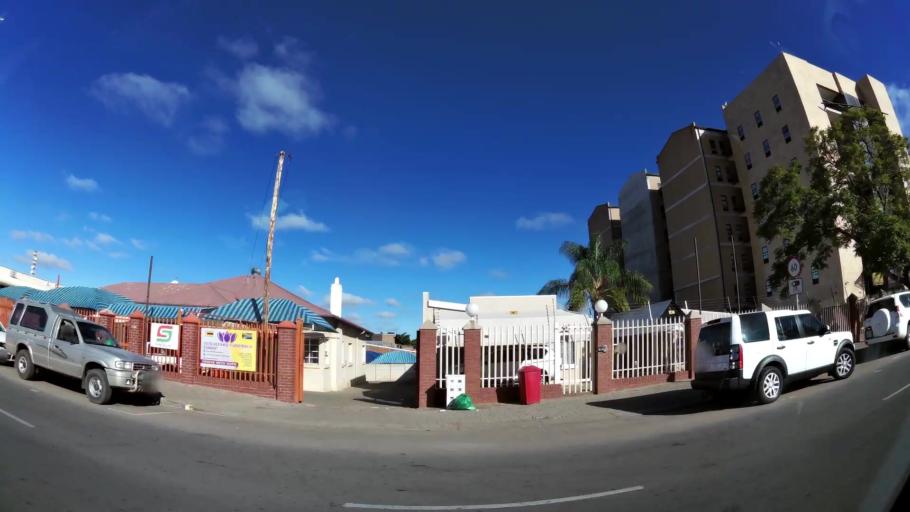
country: ZA
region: Limpopo
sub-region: Capricorn District Municipality
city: Polokwane
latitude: -23.9076
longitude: 29.4560
